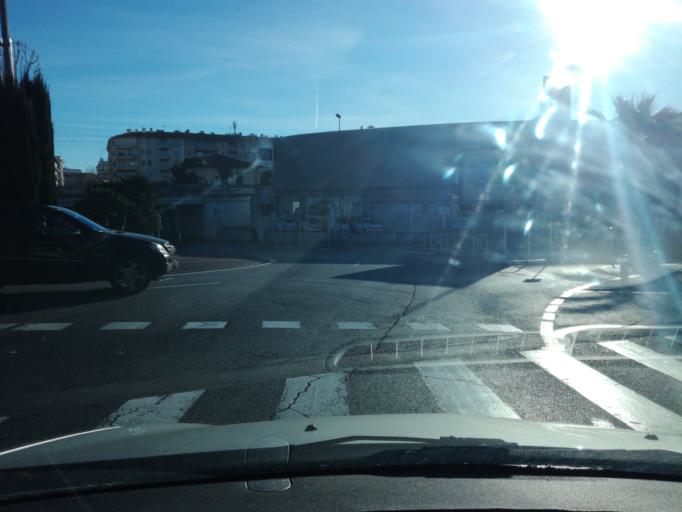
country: FR
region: Provence-Alpes-Cote d'Azur
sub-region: Departement des Alpes-Maritimes
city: Antibes
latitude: 43.5807
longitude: 7.1170
